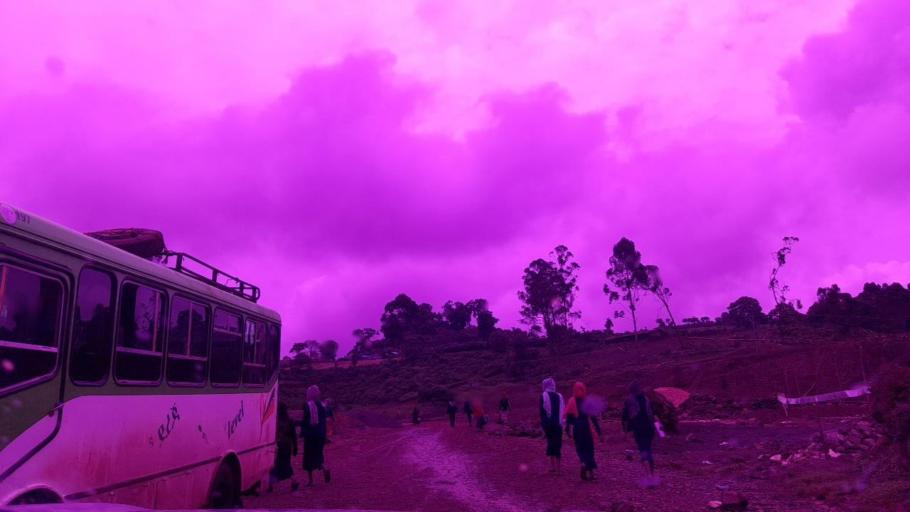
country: ET
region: Southern Nations, Nationalities, and People's Region
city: Tippi
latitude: 7.5938
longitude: 35.7623
